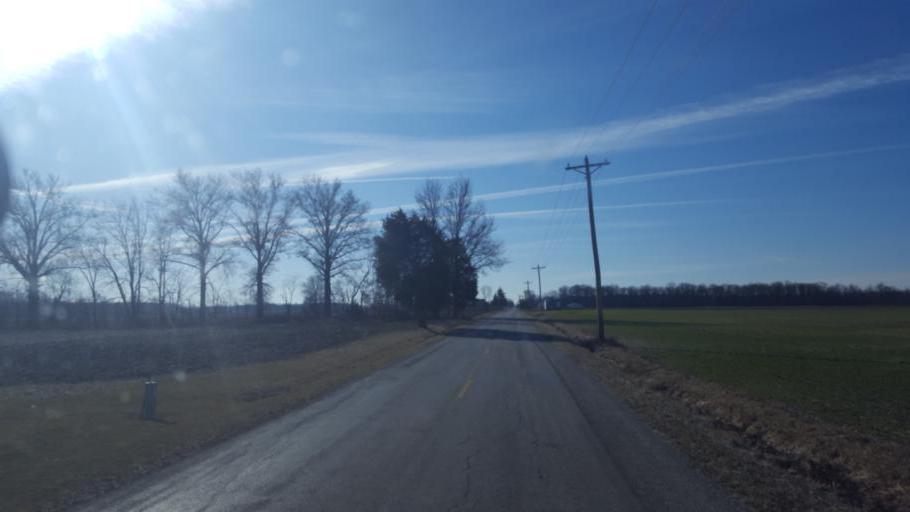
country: US
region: Ohio
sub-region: Morrow County
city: Cardington
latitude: 40.5487
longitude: -82.9956
